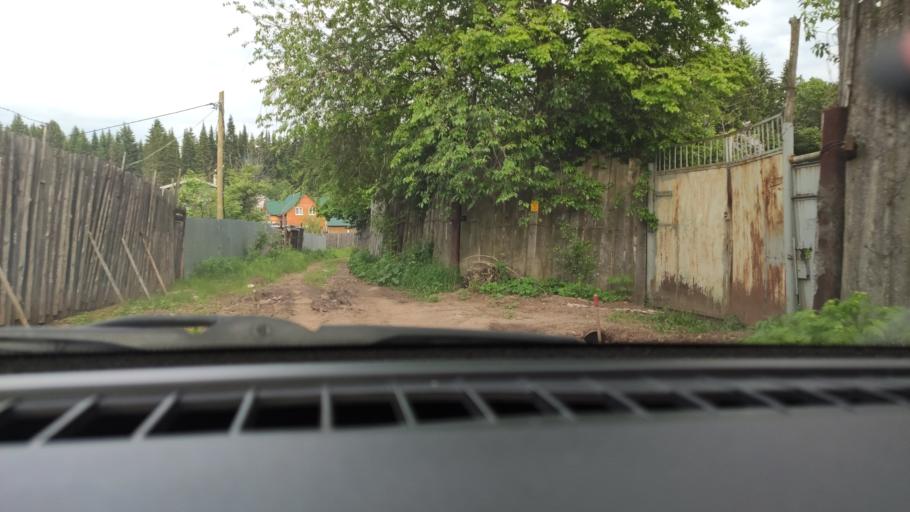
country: RU
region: Perm
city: Froly
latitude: 57.9486
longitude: 56.2820
